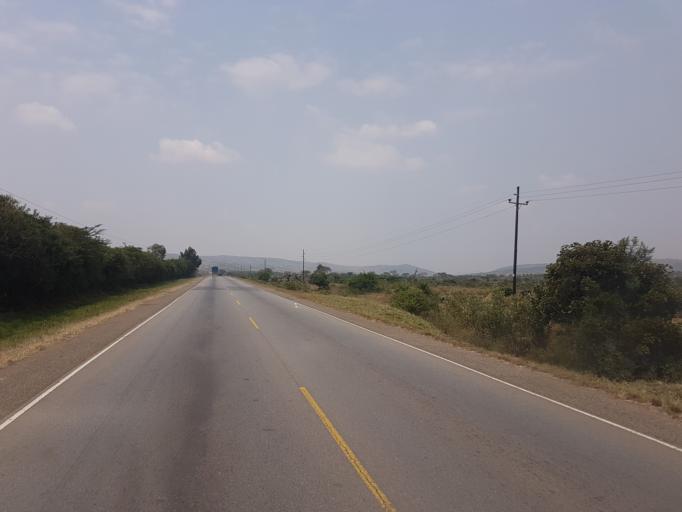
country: UG
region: Western Region
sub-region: Mbarara District
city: Mbarara
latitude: -0.5105
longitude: 30.8229
